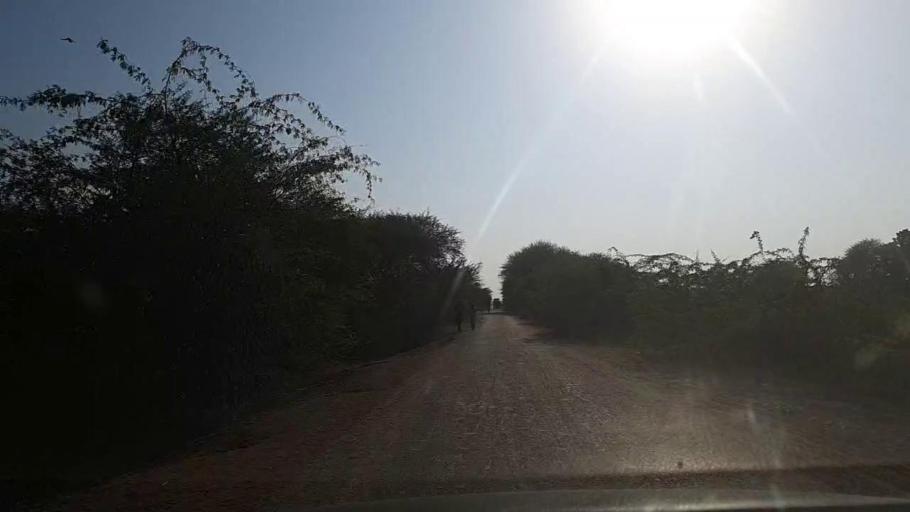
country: PK
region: Sindh
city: Naukot
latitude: 24.9963
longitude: 69.2636
